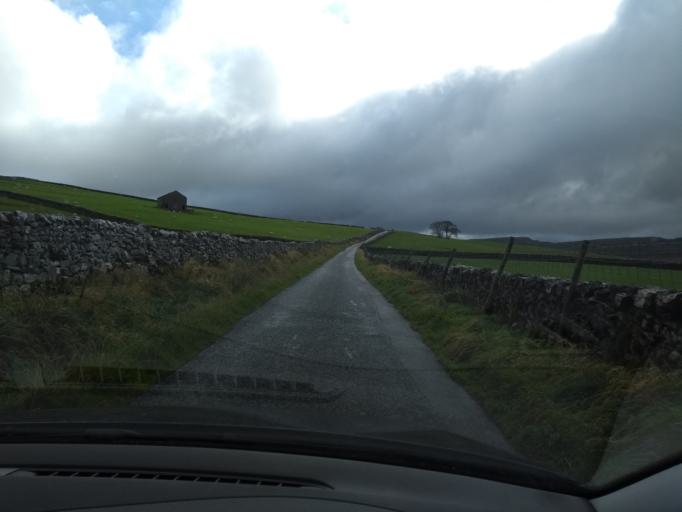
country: GB
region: England
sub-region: North Yorkshire
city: Settle
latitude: 54.1057
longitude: -2.2293
